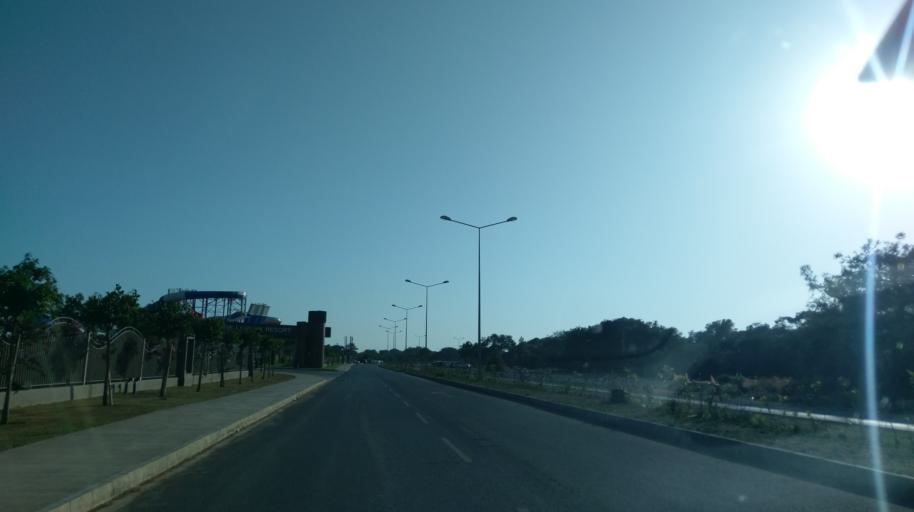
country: CY
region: Ammochostos
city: Leonarisso
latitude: 35.3562
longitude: 34.0709
